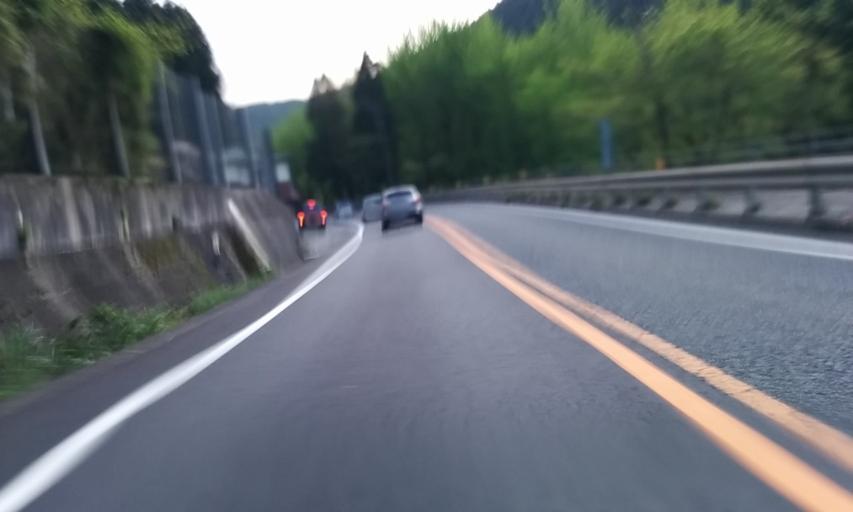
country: JP
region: Ehime
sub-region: Shikoku-chuo Shi
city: Matsuyama
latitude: 33.8173
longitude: 132.9820
